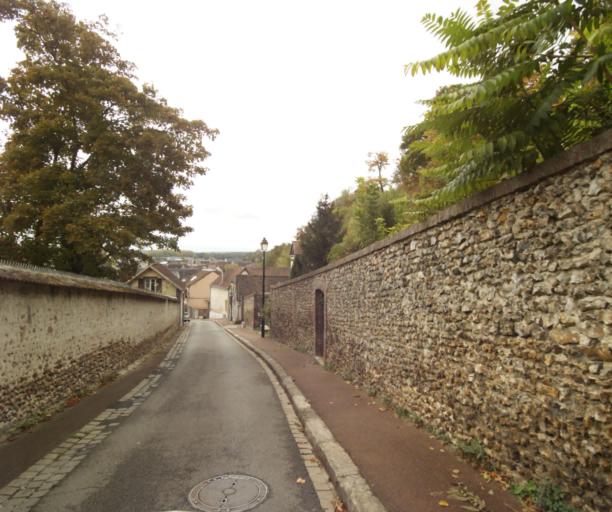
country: FR
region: Centre
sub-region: Departement d'Eure-et-Loir
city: Dreux
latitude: 48.7394
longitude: 1.3661
